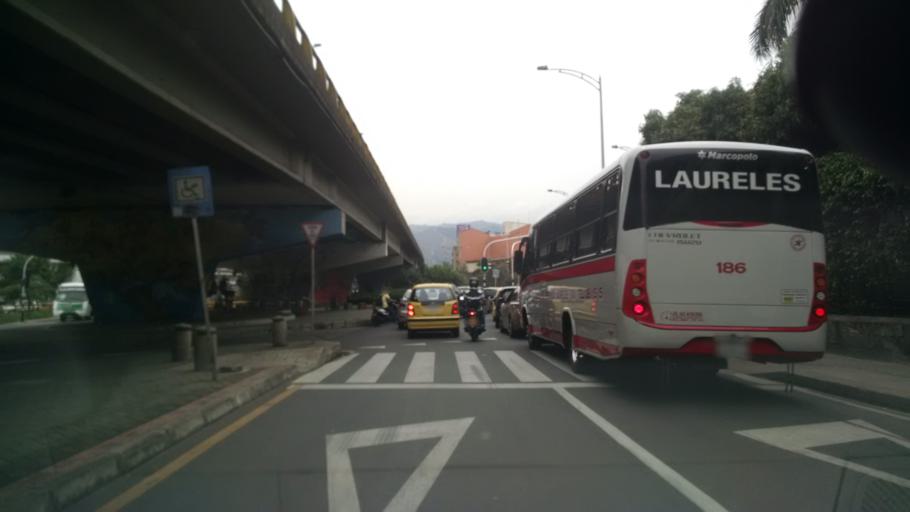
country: CO
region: Antioquia
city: Medellin
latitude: 6.2400
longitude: -75.5893
